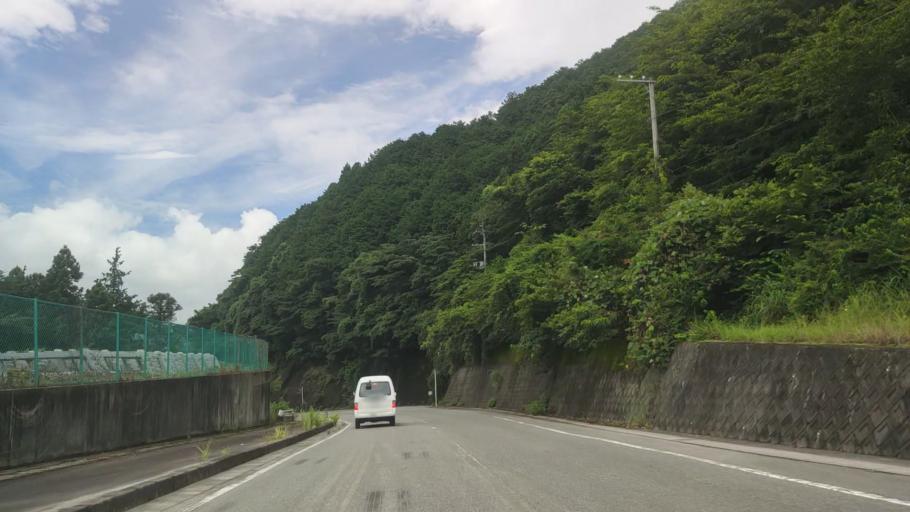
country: JP
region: Shizuoka
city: Fujinomiya
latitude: 35.2296
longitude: 138.5285
